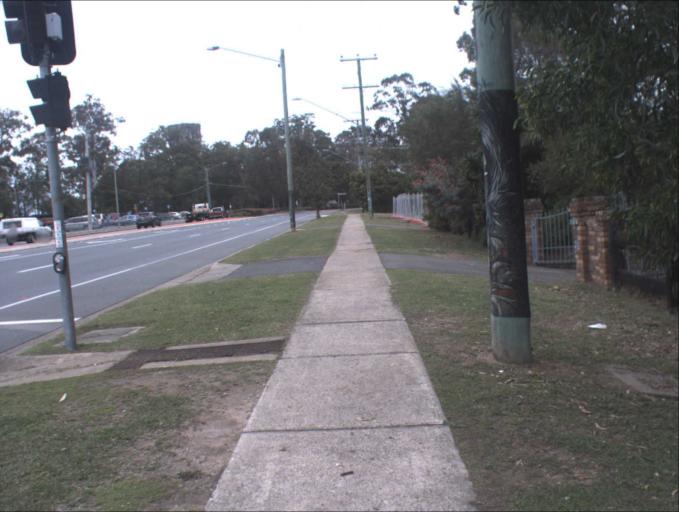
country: AU
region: Queensland
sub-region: Logan
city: Park Ridge South
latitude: -27.6830
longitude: 153.0178
